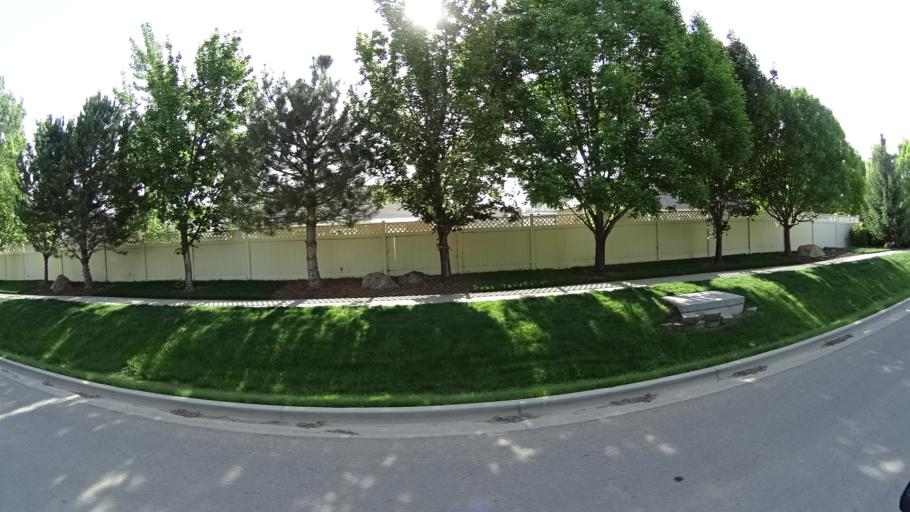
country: US
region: Idaho
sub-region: Ada County
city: Kuna
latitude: 43.5164
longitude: -116.4039
